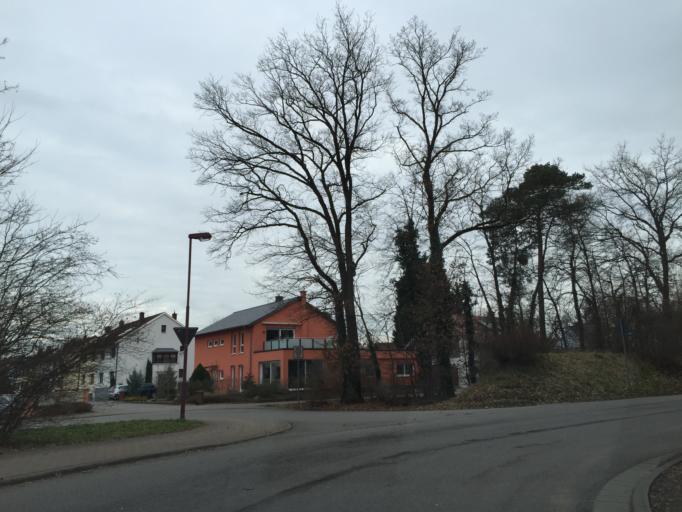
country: DE
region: Baden-Wuerttemberg
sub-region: Karlsruhe Region
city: Oftersheim
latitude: 49.3565
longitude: 8.5859
